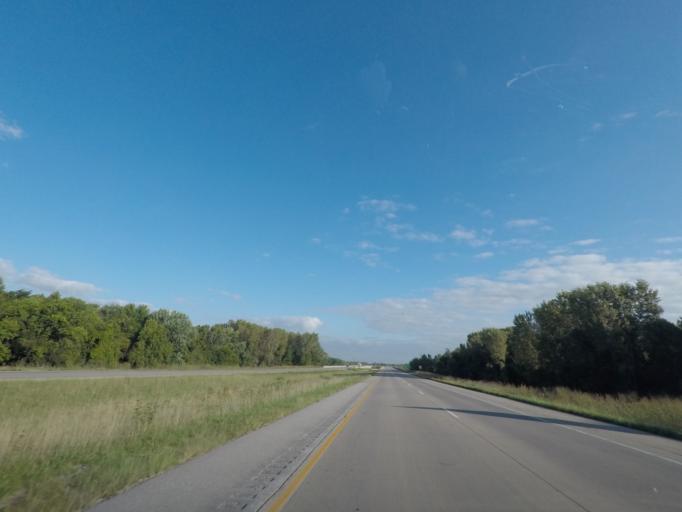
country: US
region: Iowa
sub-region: Polk County
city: Pleasant Hill
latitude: 41.5618
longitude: -93.5108
